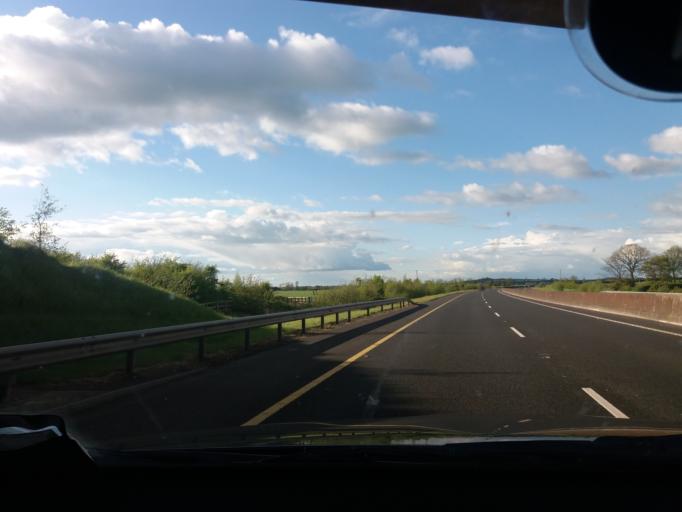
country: IE
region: Leinster
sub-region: Kildare
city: Moone
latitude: 52.9605
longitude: -6.8577
